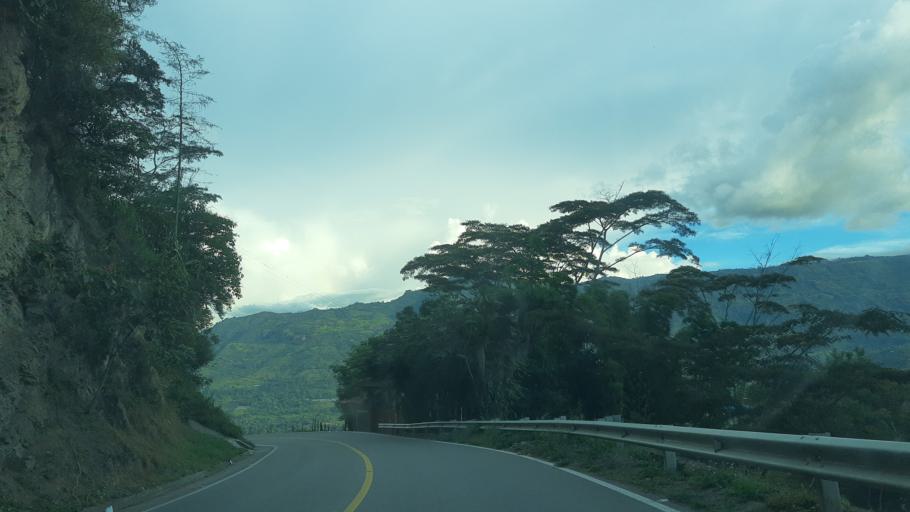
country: CO
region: Boyaca
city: Guateque
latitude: 5.0121
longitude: -73.4562
